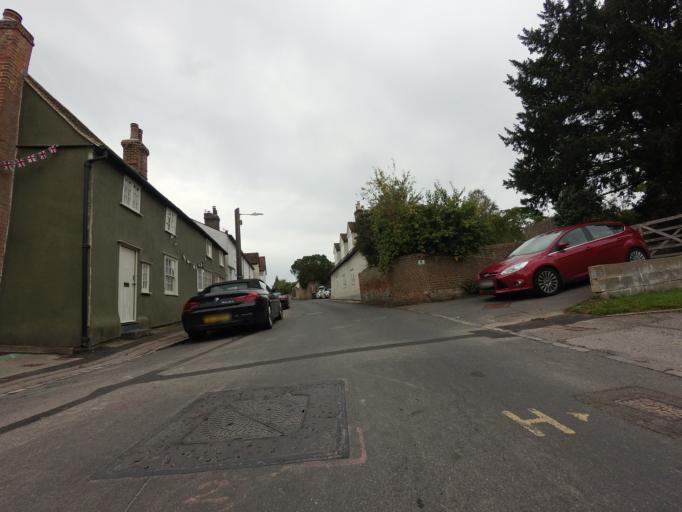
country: GB
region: England
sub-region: Essex
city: Saffron Walden
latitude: 52.0346
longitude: 0.2116
